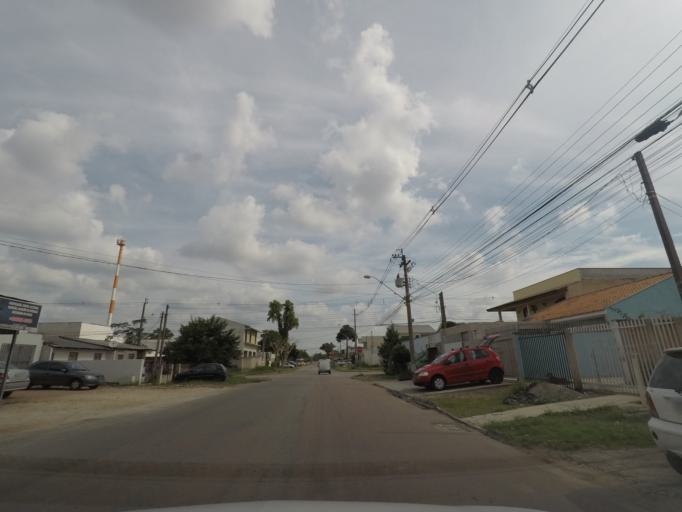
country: BR
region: Parana
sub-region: Sao Jose Dos Pinhais
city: Sao Jose dos Pinhais
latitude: -25.5017
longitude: -49.2148
